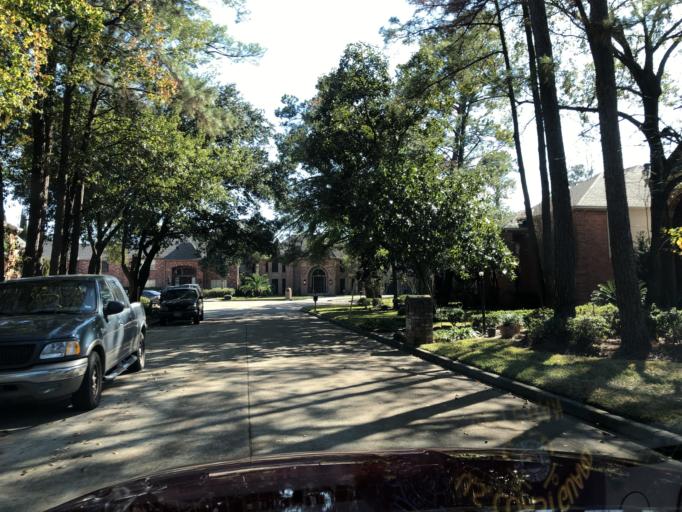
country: US
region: Texas
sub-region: Harris County
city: Tomball
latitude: 30.0238
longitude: -95.5409
